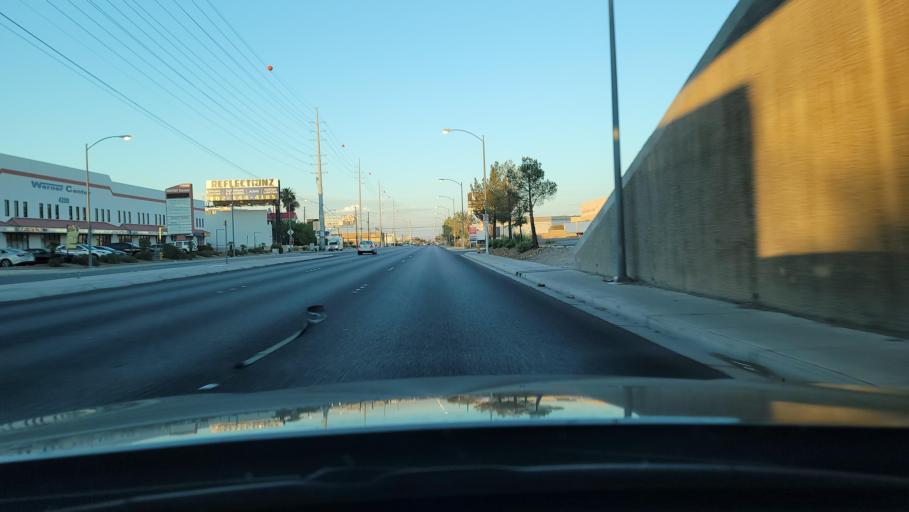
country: US
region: Nevada
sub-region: Clark County
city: Paradise
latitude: 36.0863
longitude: -115.1974
